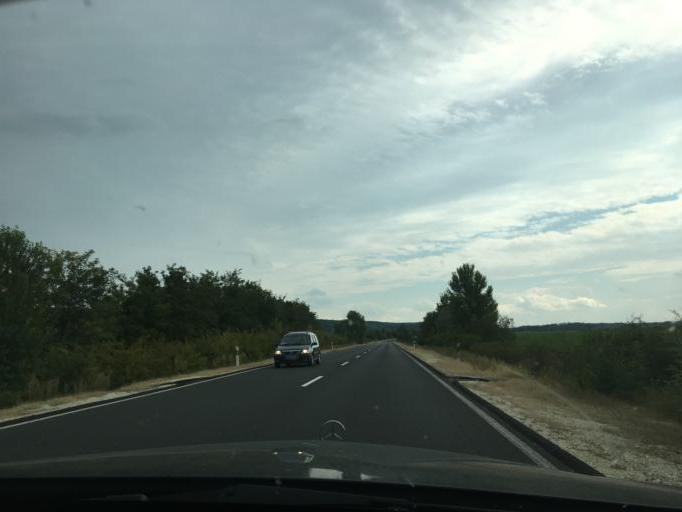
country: HU
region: Somogy
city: Balatonszarszo
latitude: 46.8299
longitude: 17.8500
